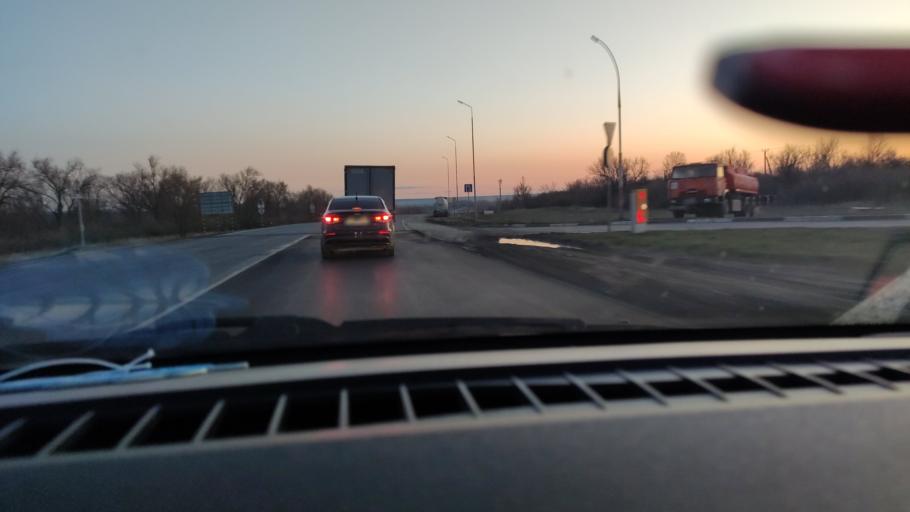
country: RU
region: Saratov
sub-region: Saratovskiy Rayon
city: Saratov
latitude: 51.6815
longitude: 46.0016
